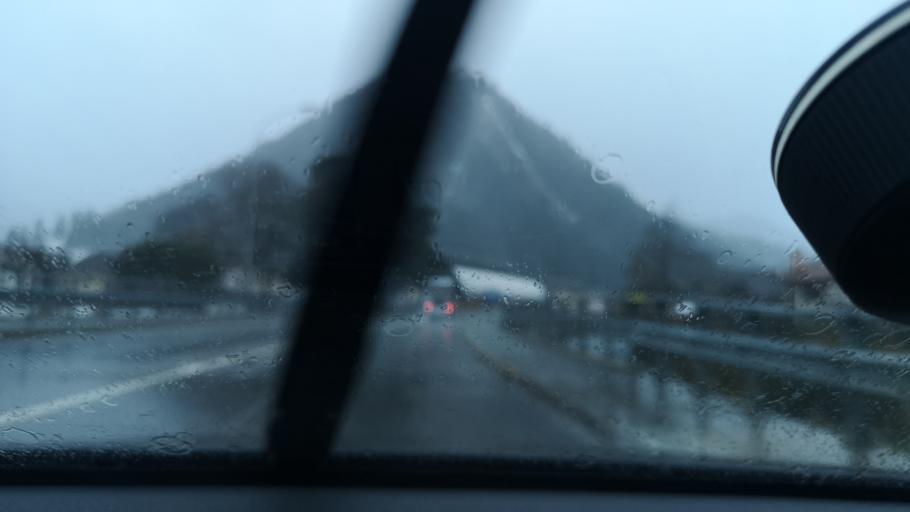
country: CH
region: Neuchatel
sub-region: Val-de-Travers District
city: Fleurier
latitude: 46.9061
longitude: 6.5803
